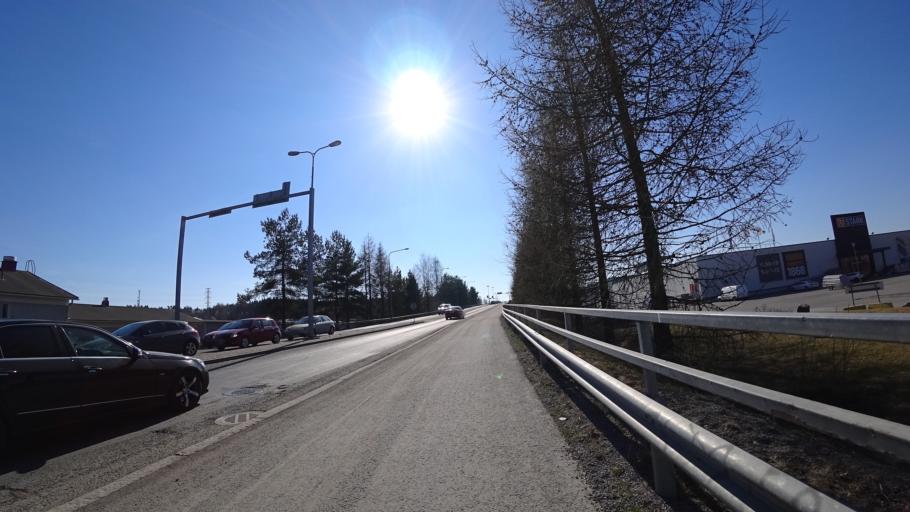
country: FI
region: Pirkanmaa
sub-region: Tampere
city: Pirkkala
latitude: 61.5217
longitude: 23.6539
